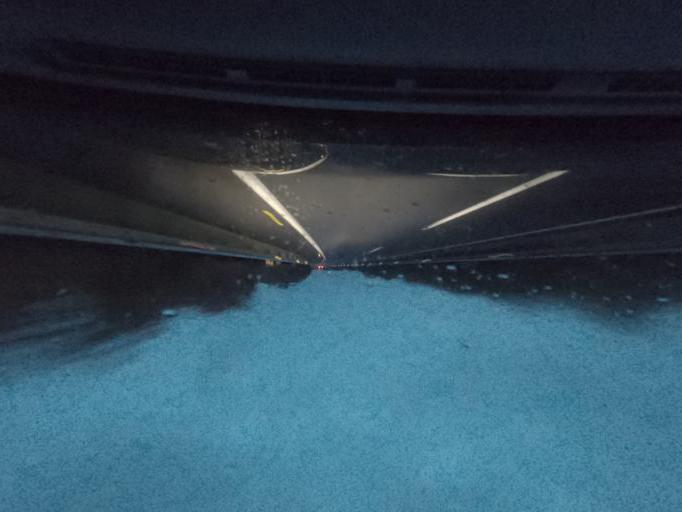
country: ES
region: Extremadura
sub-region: Provincia de Caceres
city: Aldea del Cano
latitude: 39.3489
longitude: -6.3426
